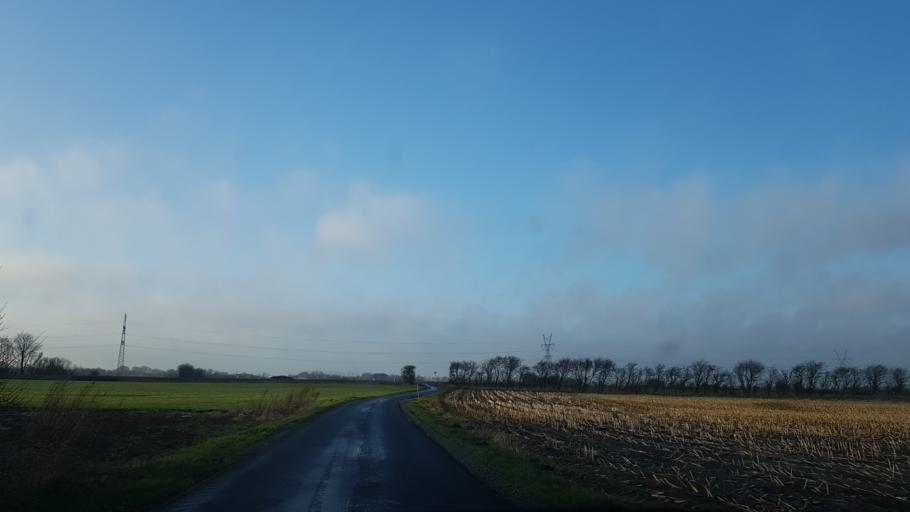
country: DK
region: South Denmark
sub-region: Aabenraa Kommune
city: Rodekro
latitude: 55.1551
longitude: 9.2990
